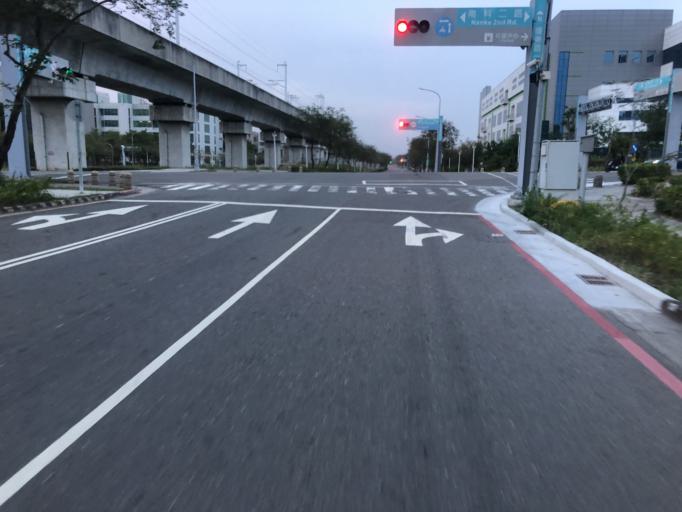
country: TW
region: Taiwan
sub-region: Tainan
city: Tainan
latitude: 23.0959
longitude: 120.2863
